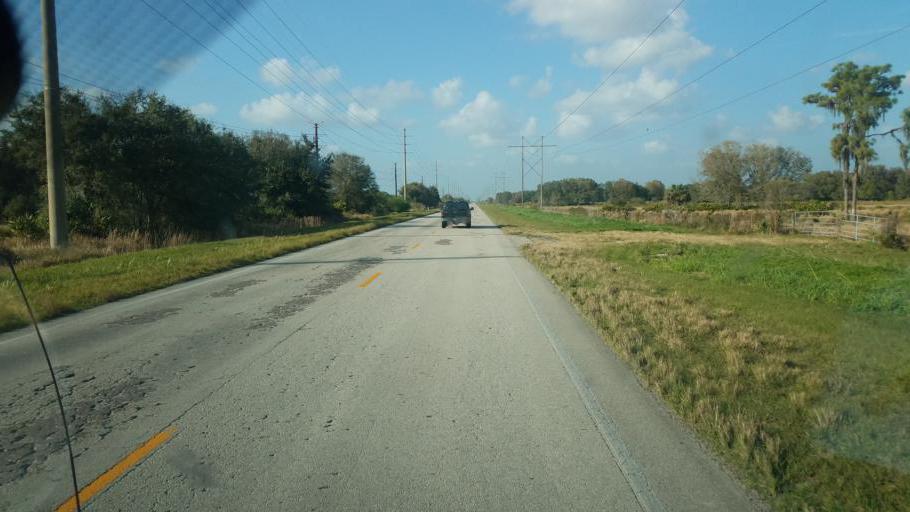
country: US
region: Florida
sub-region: Hardee County
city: Wauchula
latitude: 27.5341
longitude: -81.9287
